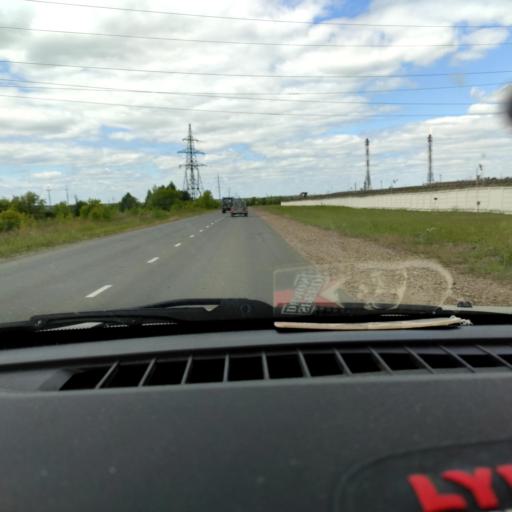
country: RU
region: Perm
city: Gamovo
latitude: 57.9104
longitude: 56.1162
